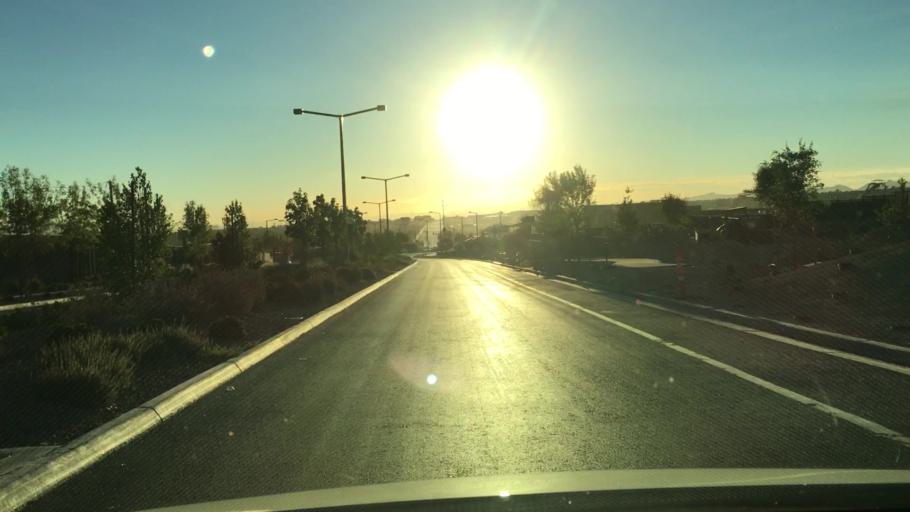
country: US
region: Nevada
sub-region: Clark County
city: Summerlin South
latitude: 36.0626
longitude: -115.3123
